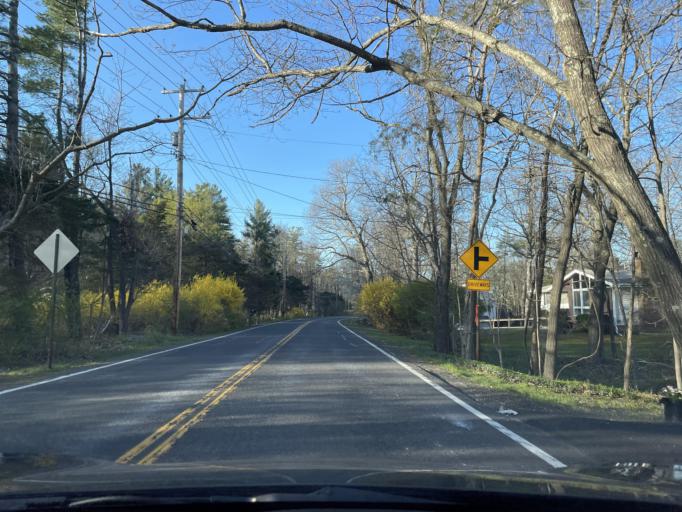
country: US
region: New York
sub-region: Ulster County
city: Woodstock
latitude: 42.0200
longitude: -74.1111
